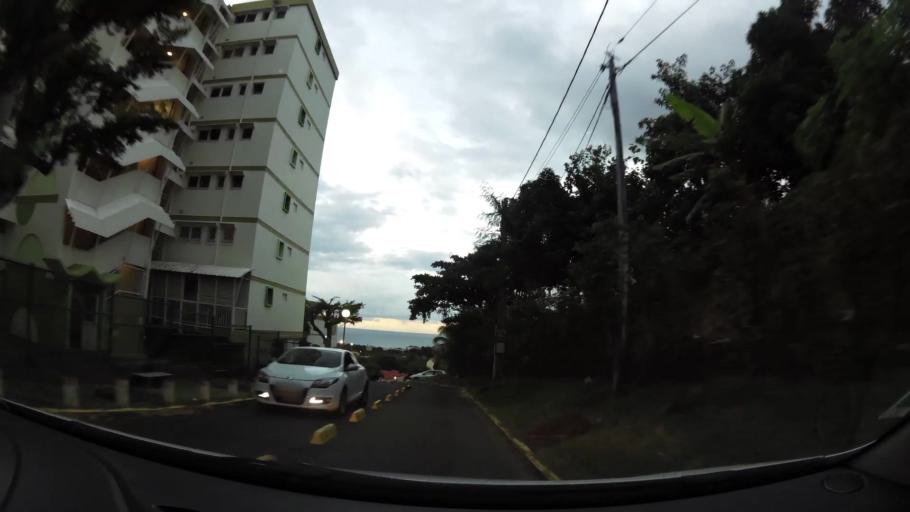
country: RE
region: Reunion
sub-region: Reunion
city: Saint-Denis
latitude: -20.8990
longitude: 55.4703
